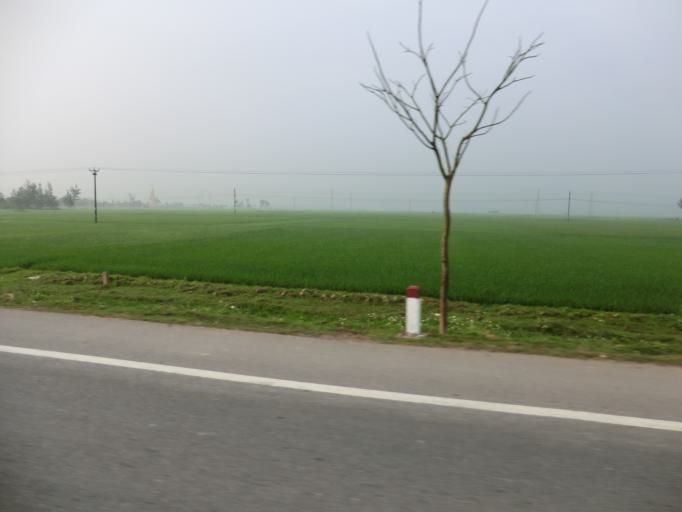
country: VN
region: Ha Tinh
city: Cam Xuyen
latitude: 18.2312
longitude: 106.0349
